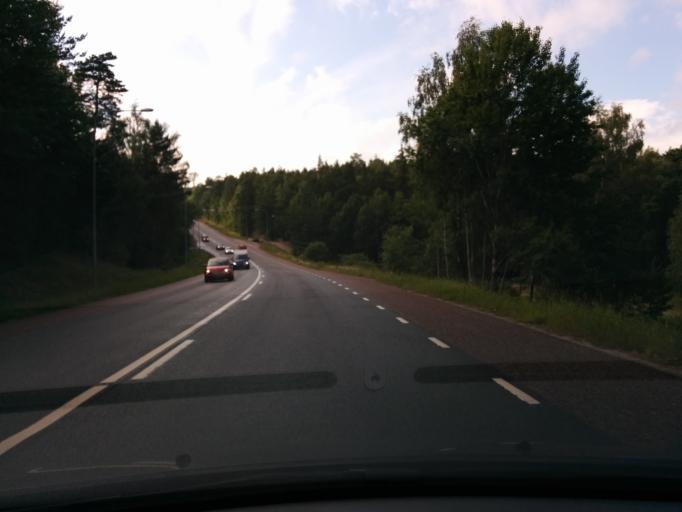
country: SE
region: Stockholm
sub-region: Sollentuna Kommun
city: Sollentuna
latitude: 59.4364
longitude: 17.9907
